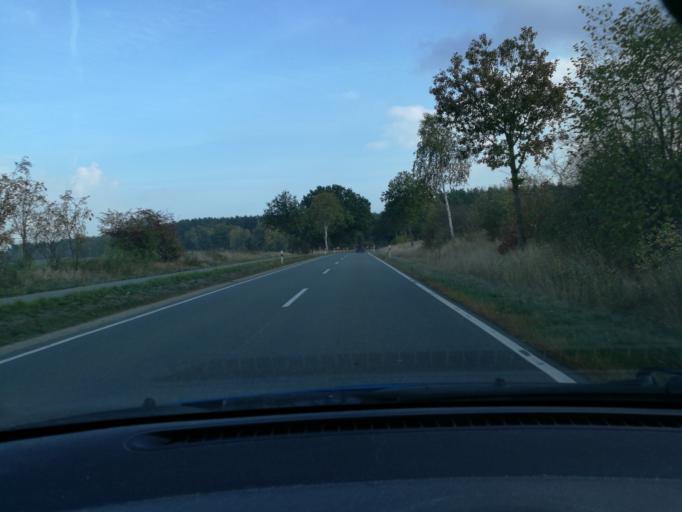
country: DE
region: Lower Saxony
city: Karwitz
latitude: 53.1279
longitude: 10.9721
